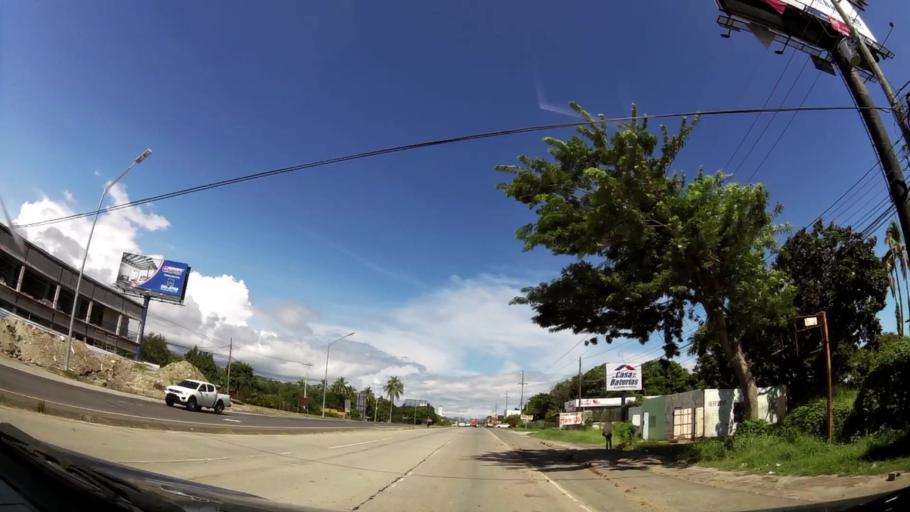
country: PA
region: Panama
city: Nueva Gorgona
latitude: 8.5467
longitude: -79.9115
